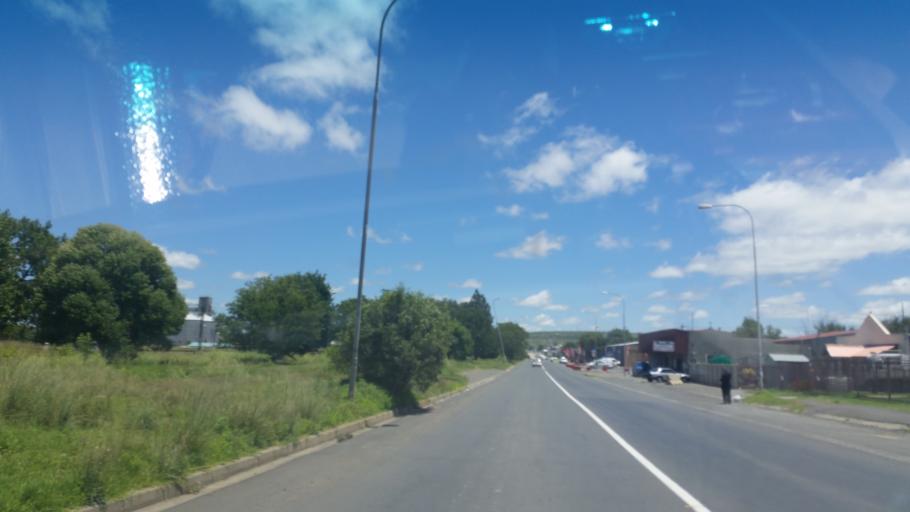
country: ZA
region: Orange Free State
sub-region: Thabo Mofutsanyana District Municipality
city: Harrismith
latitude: -28.2787
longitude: 29.1272
